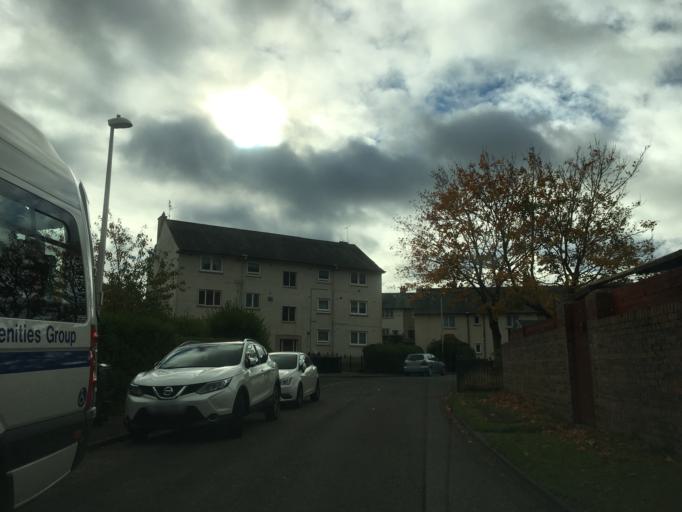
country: GB
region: Scotland
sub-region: Midlothian
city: Loanhead
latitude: 55.9185
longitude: -3.1603
